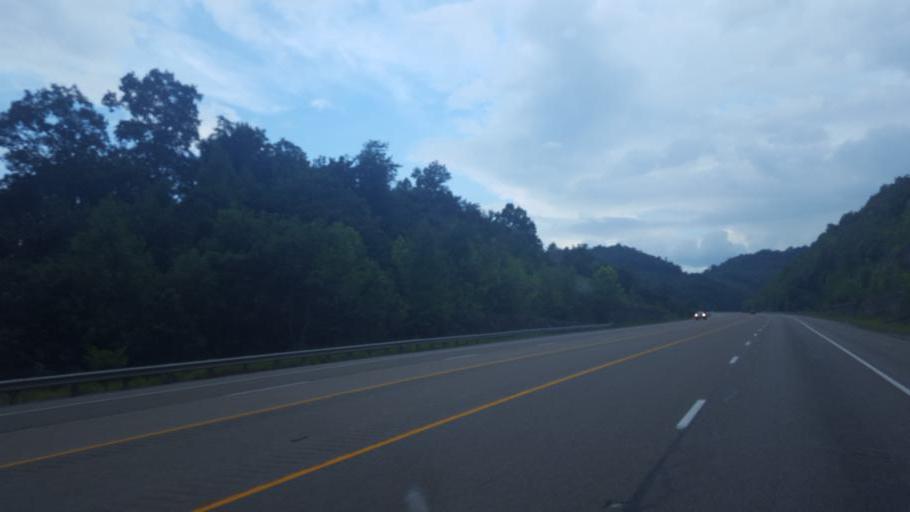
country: US
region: Kentucky
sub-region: Letcher County
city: Jenkins
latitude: 37.2294
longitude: -82.6253
